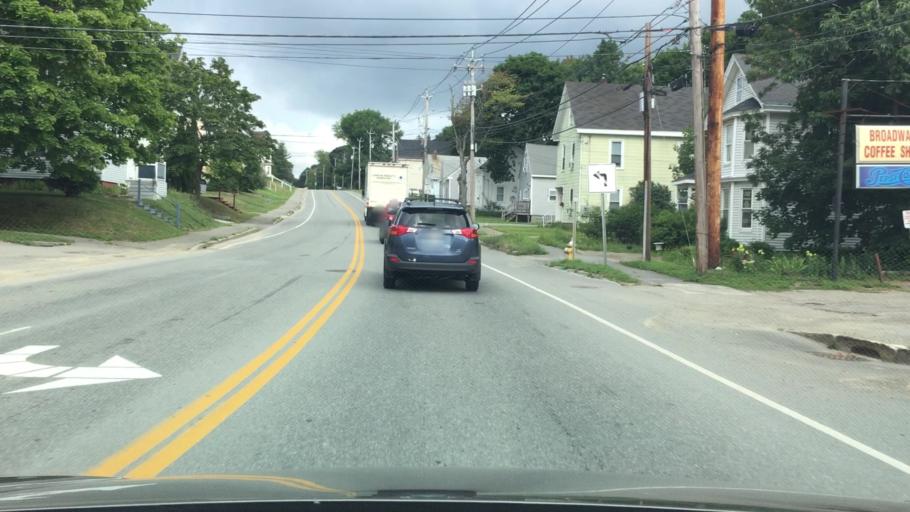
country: US
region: Maine
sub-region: Penobscot County
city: Bangor
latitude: 44.8125
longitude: -68.7702
